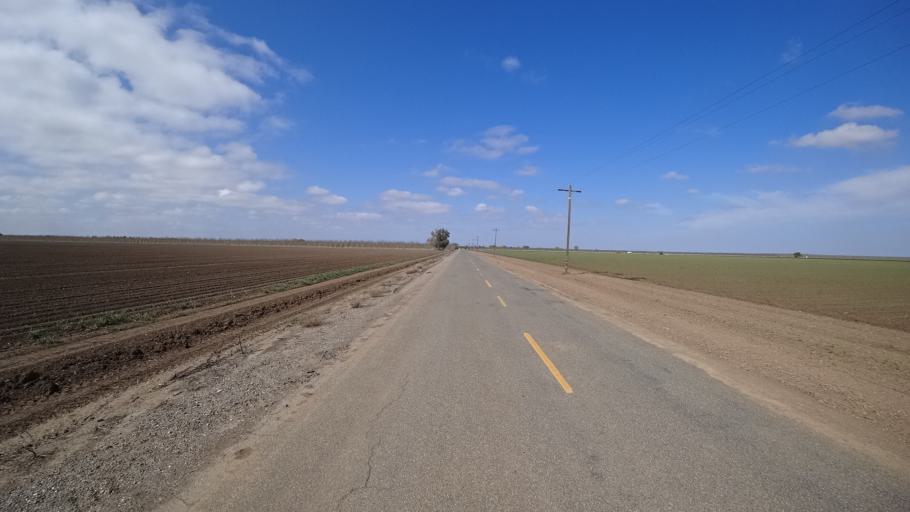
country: US
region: California
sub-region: Colusa County
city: Colusa
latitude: 39.4202
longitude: -121.9349
